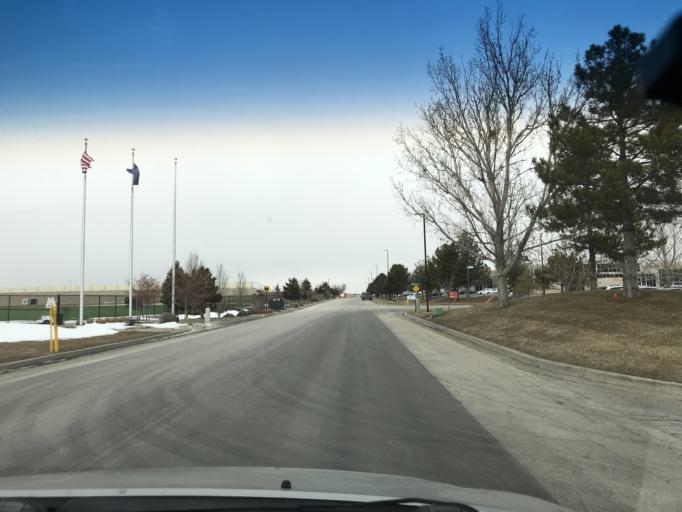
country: US
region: Utah
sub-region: Salt Lake County
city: West Valley City
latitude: 40.7807
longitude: -112.0362
